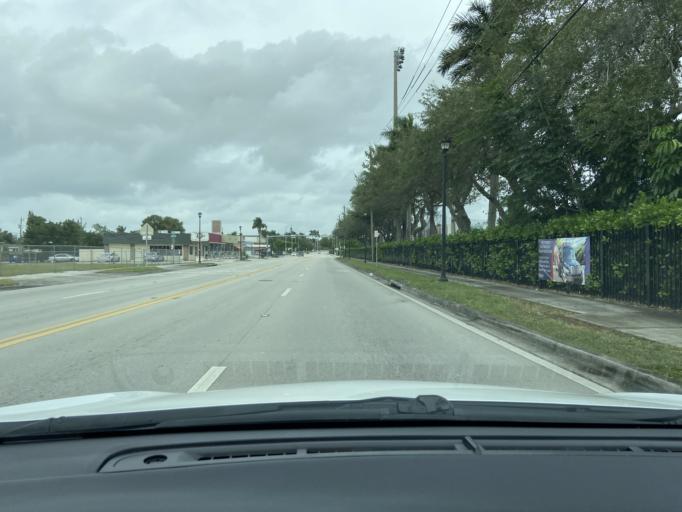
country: US
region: Florida
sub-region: Miami-Dade County
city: Biscayne Park
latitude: 25.8741
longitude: -80.1857
